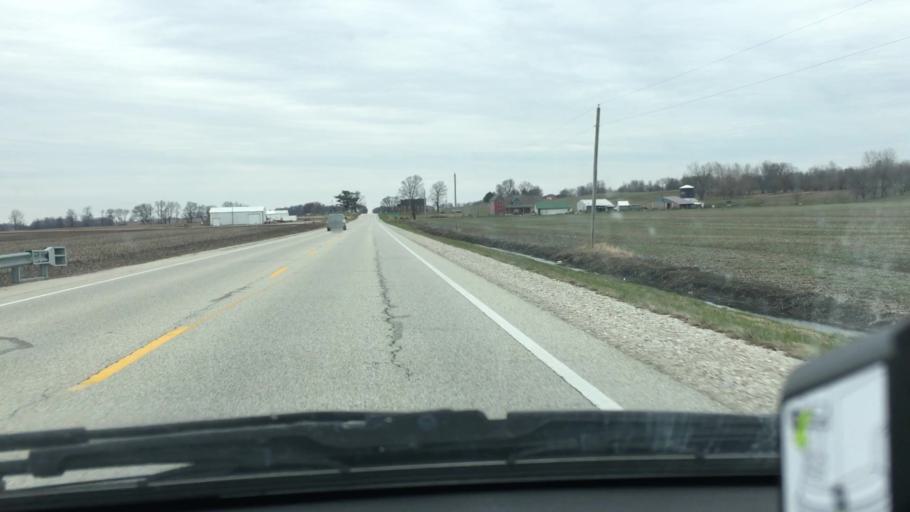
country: US
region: Indiana
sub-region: Greene County
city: Bloomfield
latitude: 38.9716
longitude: -87.0165
